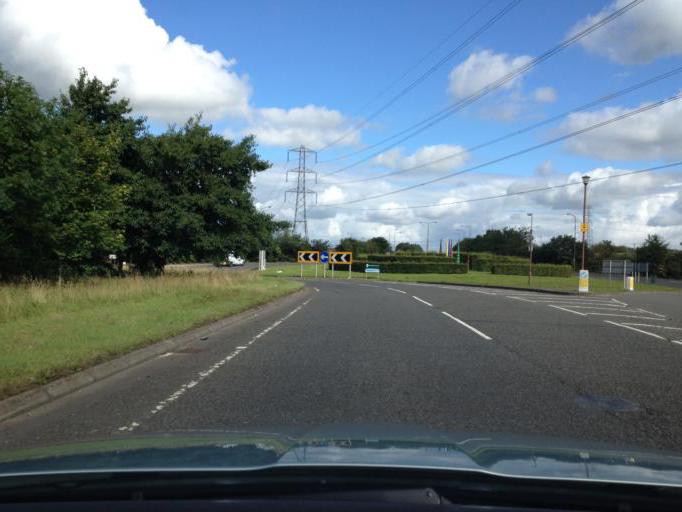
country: GB
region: Scotland
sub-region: West Lothian
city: Armadale
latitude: 55.8991
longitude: -3.6773
